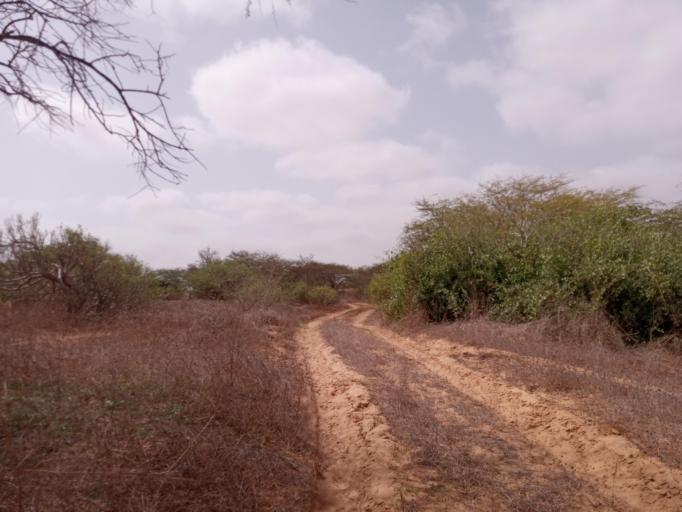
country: SN
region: Saint-Louis
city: Saint-Louis
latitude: 15.9217
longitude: -16.4527
